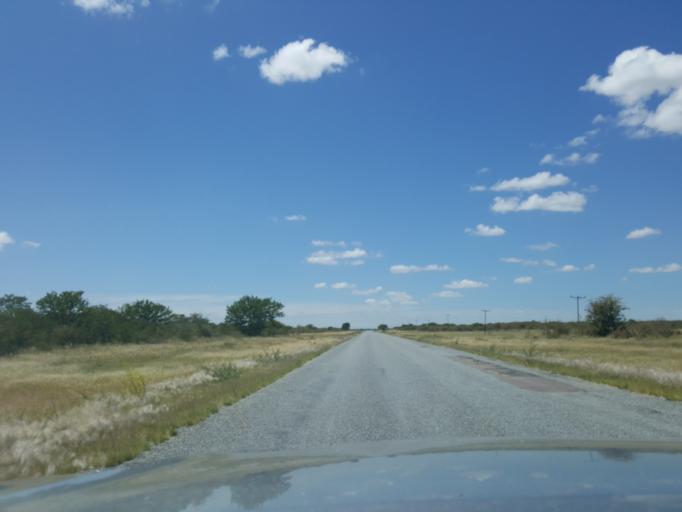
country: BW
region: Central
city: Gweta
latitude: -20.1364
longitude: 25.6595
